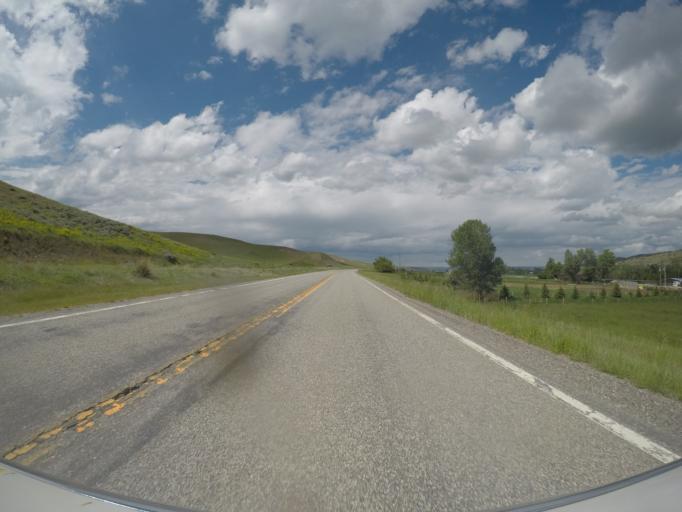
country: US
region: Montana
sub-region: Sweet Grass County
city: Big Timber
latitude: 45.7502
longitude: -109.9939
